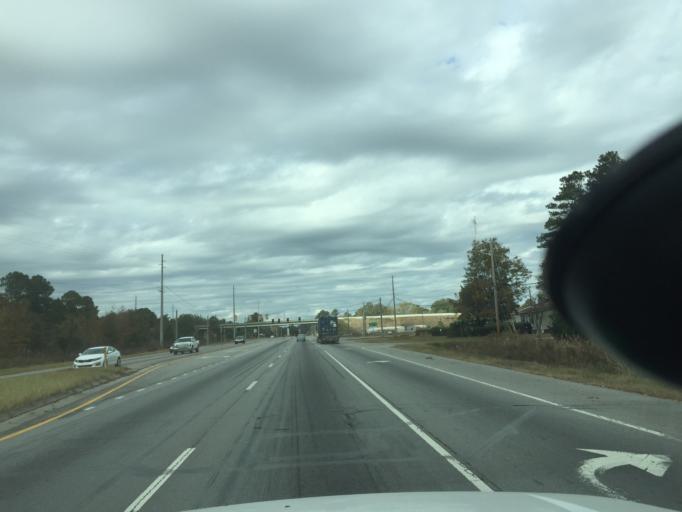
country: US
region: Georgia
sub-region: Chatham County
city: Port Wentworth
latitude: 32.1603
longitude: -81.1831
